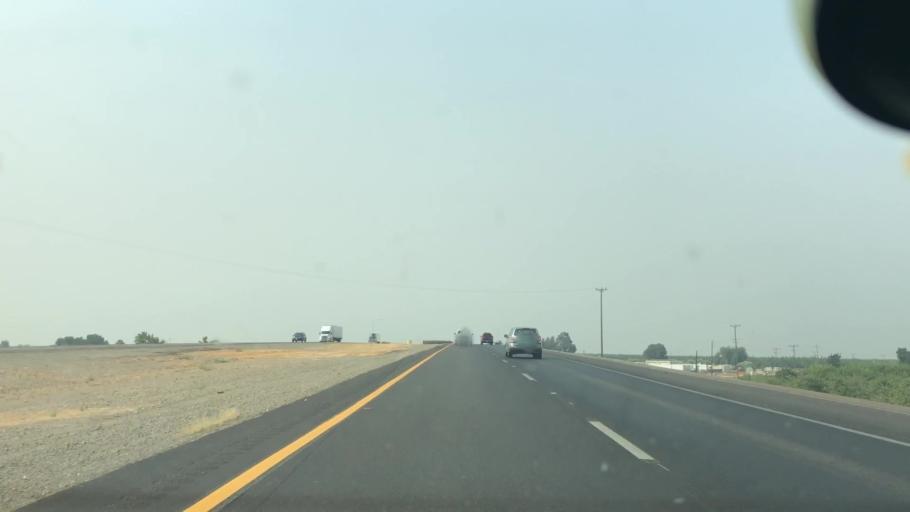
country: US
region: California
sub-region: San Joaquin County
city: Tracy
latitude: 37.6785
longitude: -121.3431
